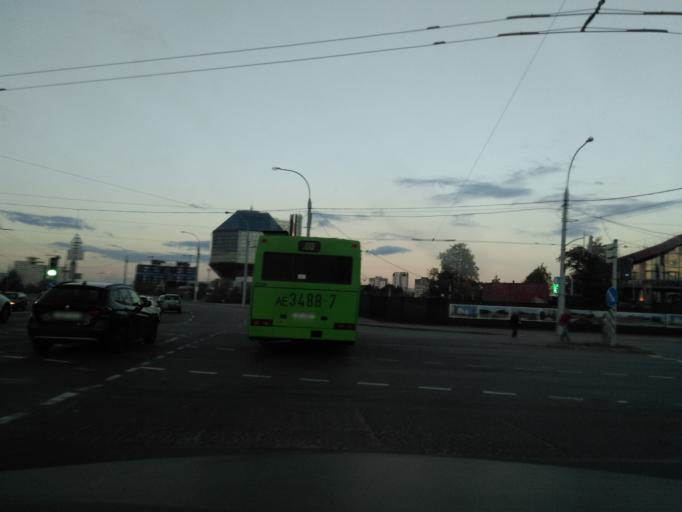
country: BY
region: Minsk
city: Minsk
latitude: 53.9299
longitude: 27.6389
